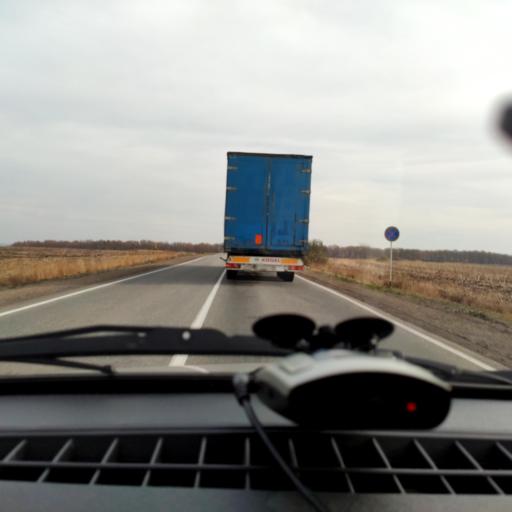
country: RU
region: Voronezj
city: Shilovo
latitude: 51.4518
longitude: 38.9814
